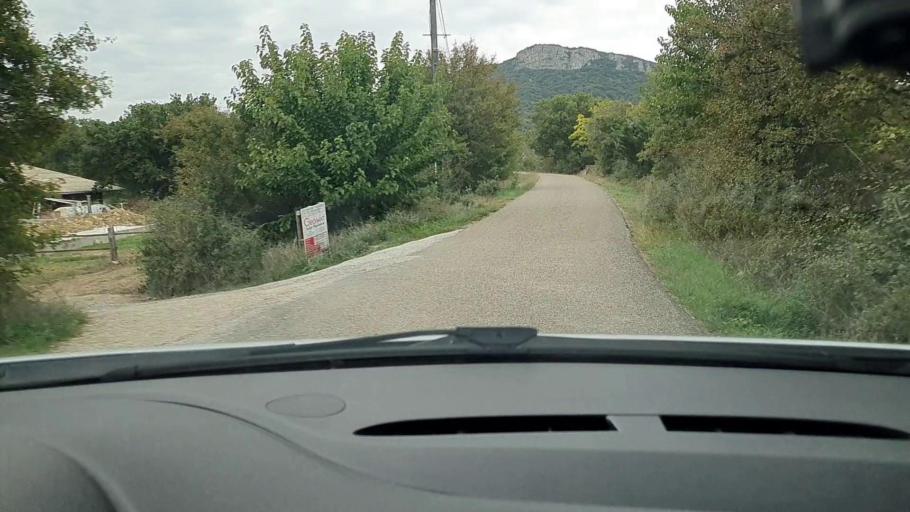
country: FR
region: Languedoc-Roussillon
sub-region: Departement du Gard
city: Mons
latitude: 44.1582
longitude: 4.2902
